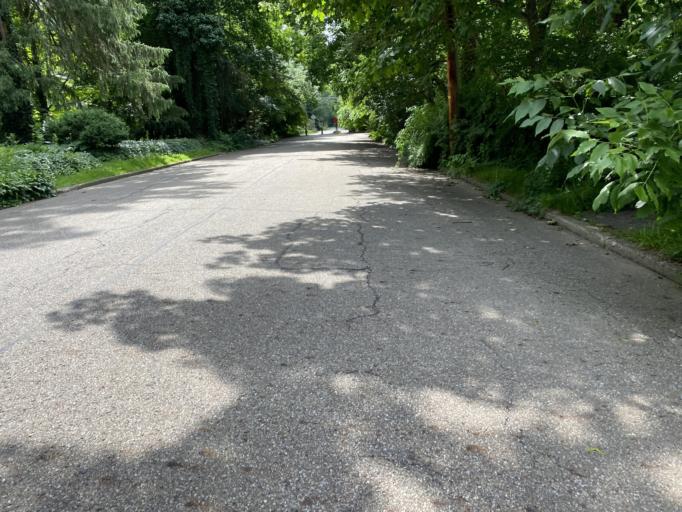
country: US
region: Ohio
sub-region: Summit County
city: Fairlawn
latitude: 41.1145
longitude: -81.5837
